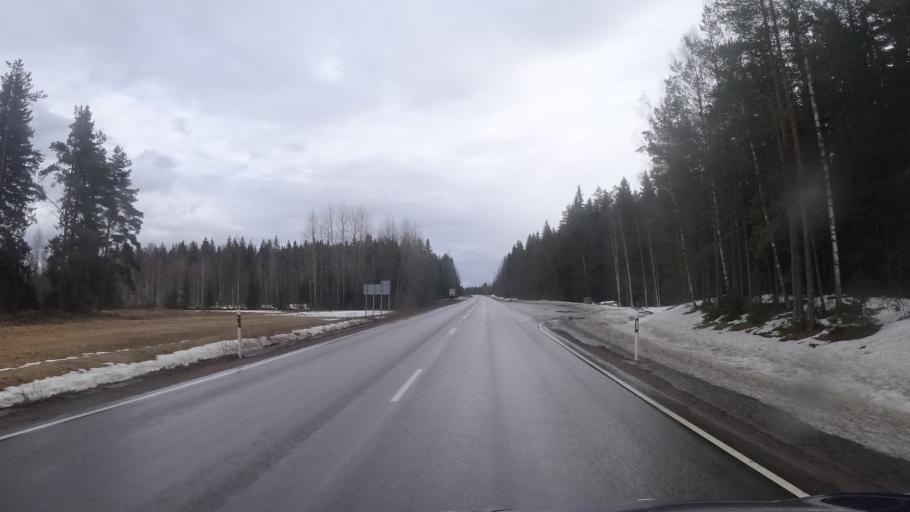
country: FI
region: Kymenlaakso
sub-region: Kouvola
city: Elimaeki
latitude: 60.6904
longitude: 26.5753
